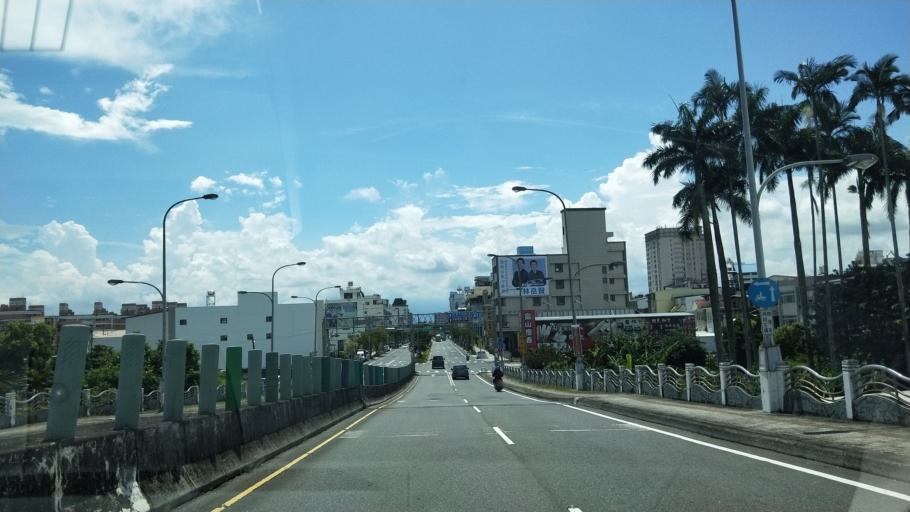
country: TW
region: Taiwan
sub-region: Yilan
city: Yilan
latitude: 24.7620
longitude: 121.7604
